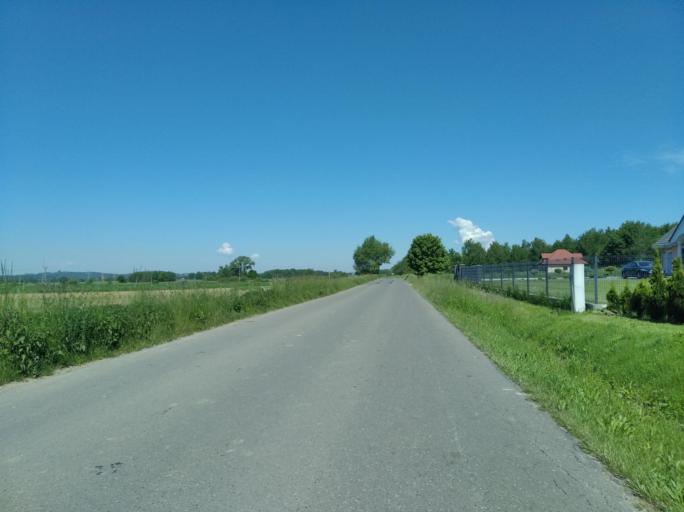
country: PL
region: Subcarpathian Voivodeship
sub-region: Powiat krosnienski
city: Odrzykon
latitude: 49.7254
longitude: 21.7607
